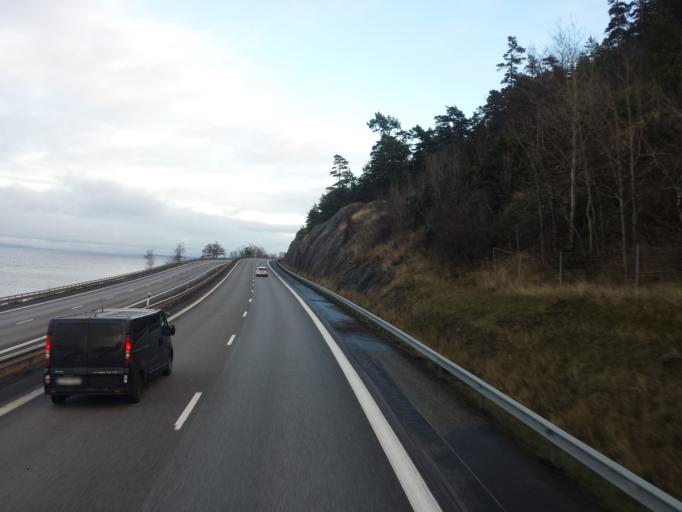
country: SE
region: Joenkoeping
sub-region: Jonkopings Kommun
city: Kaxholmen
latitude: 57.8673
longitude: 14.2708
